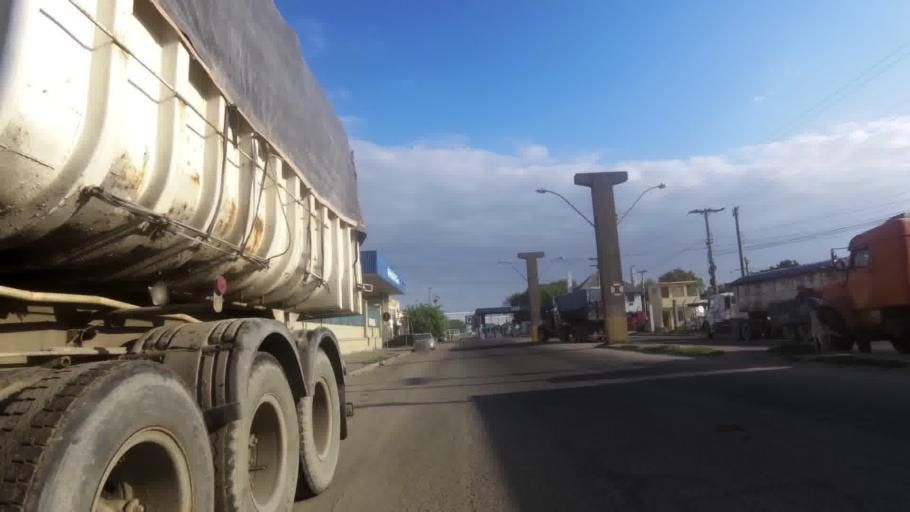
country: BR
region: Rio Grande do Sul
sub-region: Rio Grande
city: Rio Grande
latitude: -32.0446
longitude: -52.0758
